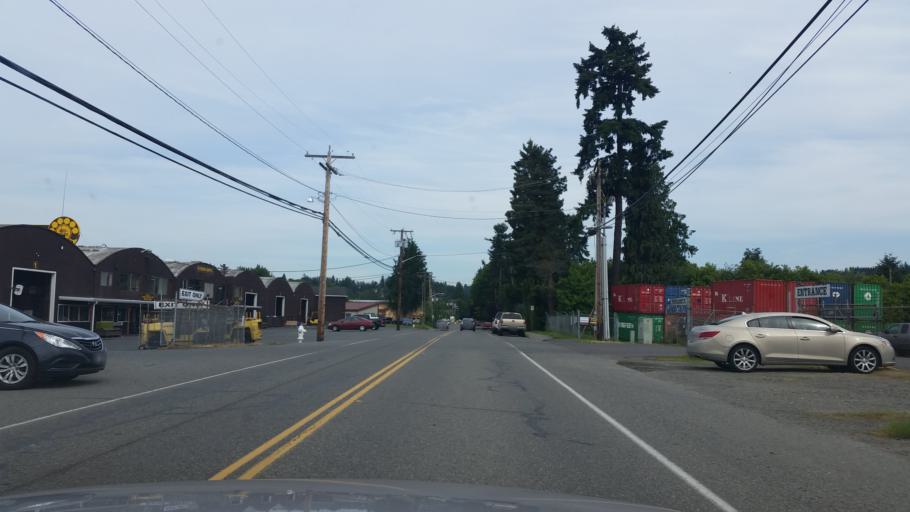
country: US
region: Washington
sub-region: King County
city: Kenmore
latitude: 47.7571
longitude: -122.2470
